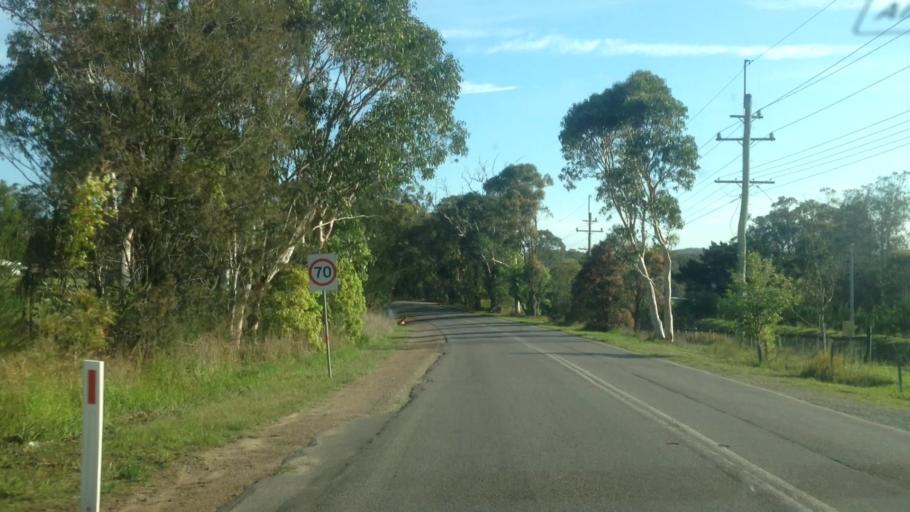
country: AU
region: New South Wales
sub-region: Lake Macquarie Shire
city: Dora Creek
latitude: -33.1063
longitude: 151.4768
